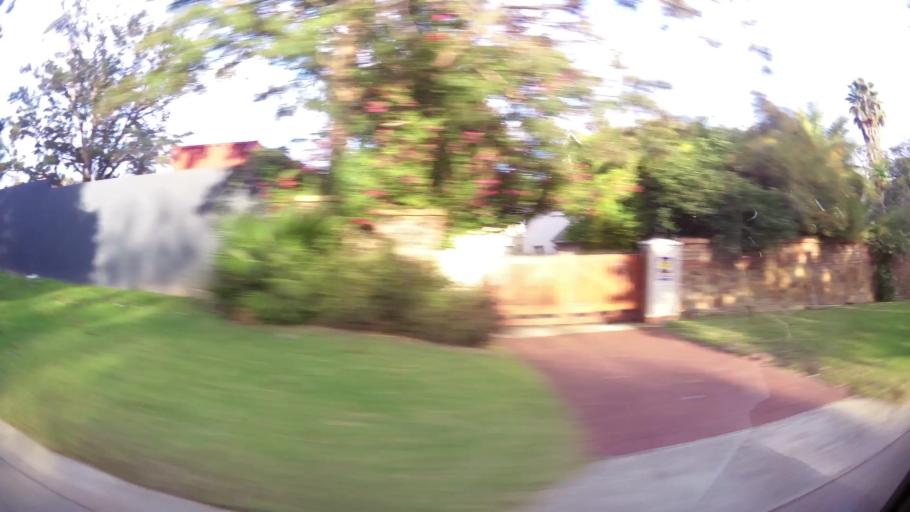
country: ZA
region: Eastern Cape
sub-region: Nelson Mandela Bay Metropolitan Municipality
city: Port Elizabeth
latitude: -33.9797
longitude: 25.5795
